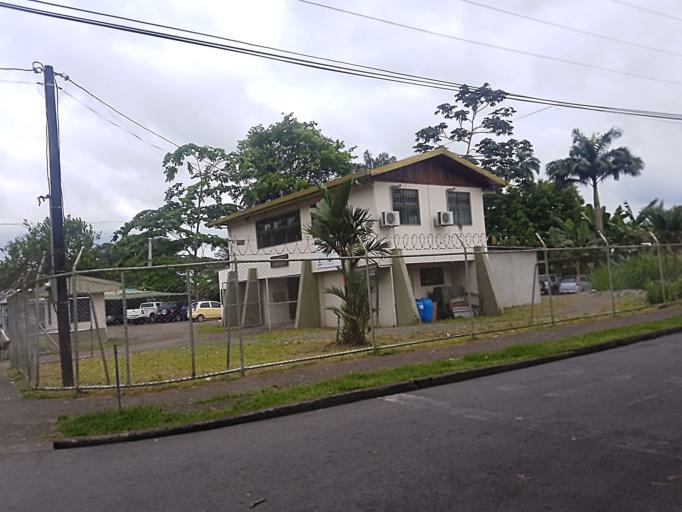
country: CR
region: Heredia
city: La Virgen
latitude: 10.4565
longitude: -84.0078
